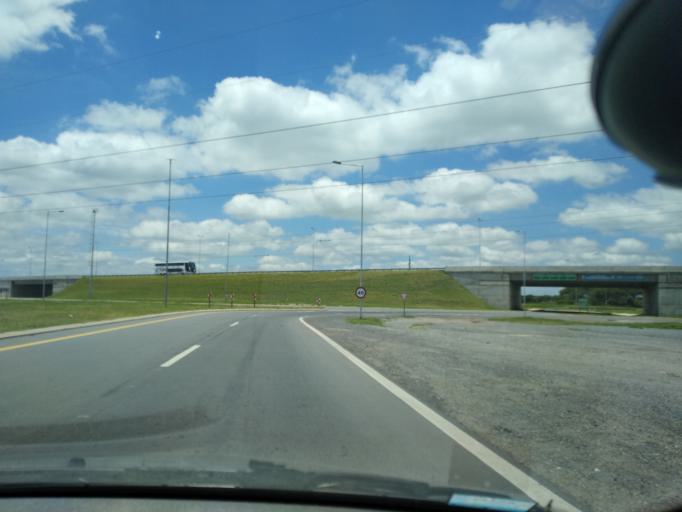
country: AR
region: Cordoba
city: Alta Gracia
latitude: -31.6522
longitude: -64.3169
